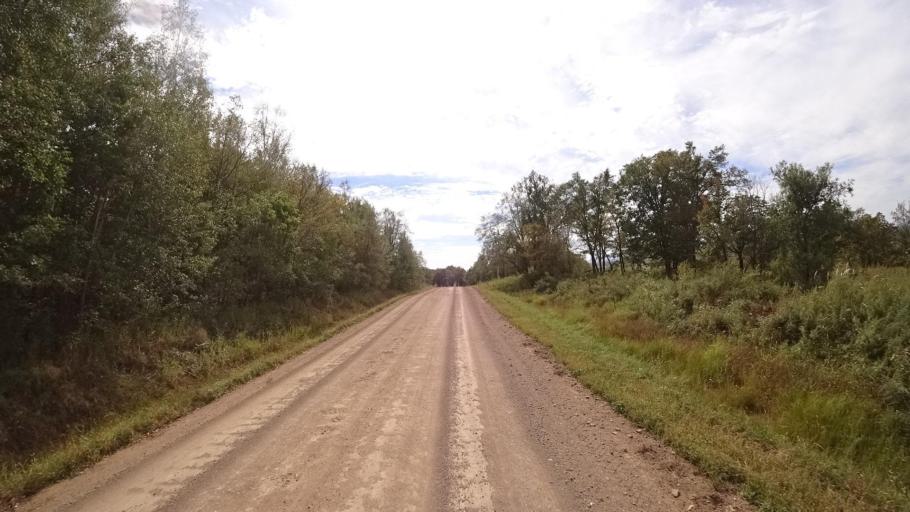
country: RU
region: Primorskiy
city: Yakovlevka
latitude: 44.5747
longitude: 133.5939
